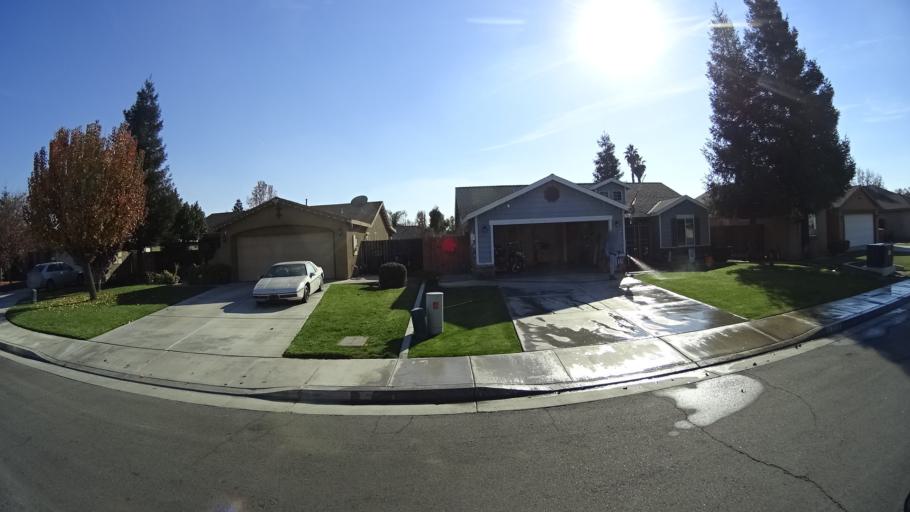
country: US
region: California
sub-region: Kern County
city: Greenfield
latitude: 35.2999
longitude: -119.0443
